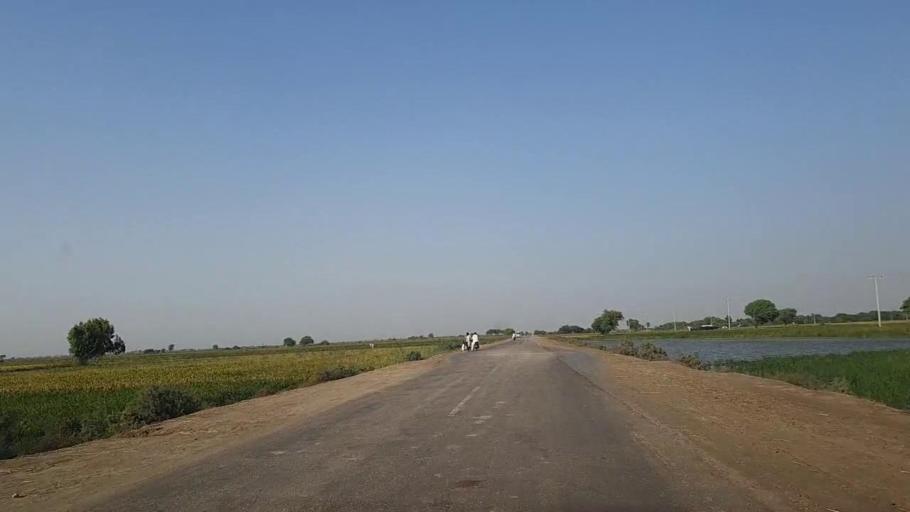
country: PK
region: Sindh
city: Mirpur Batoro
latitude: 24.5886
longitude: 68.3977
